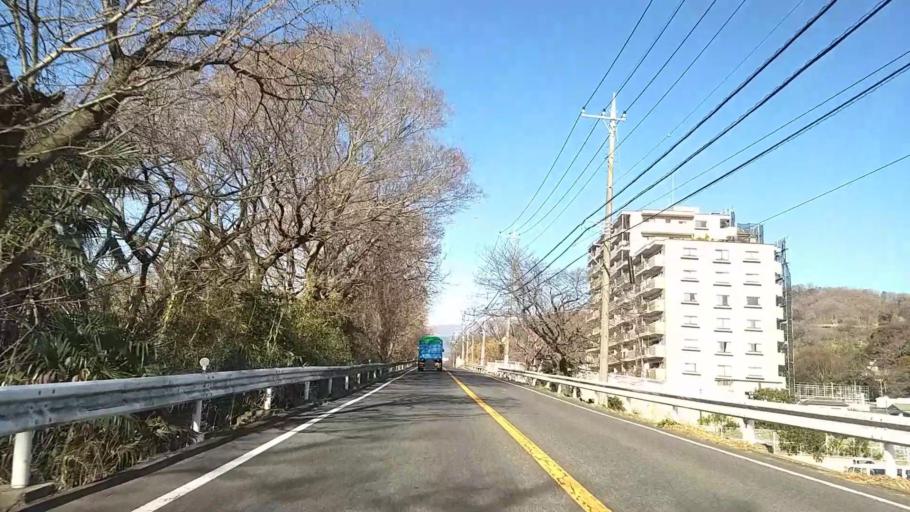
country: JP
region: Kanagawa
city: Hadano
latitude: 35.3622
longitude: 139.2478
